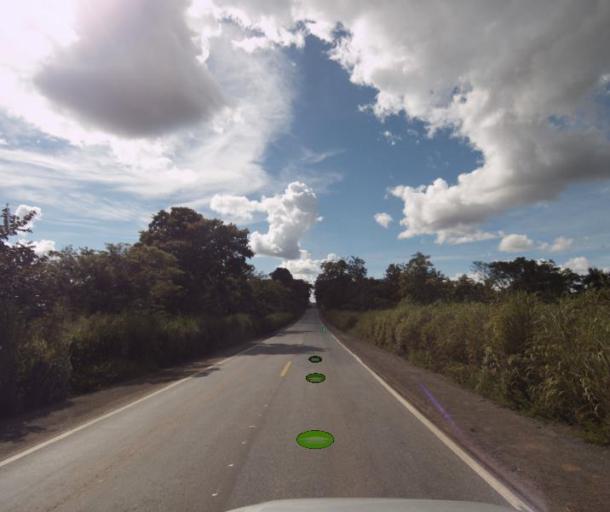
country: BR
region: Goias
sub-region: Porangatu
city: Porangatu
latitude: -13.1324
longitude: -49.1931
